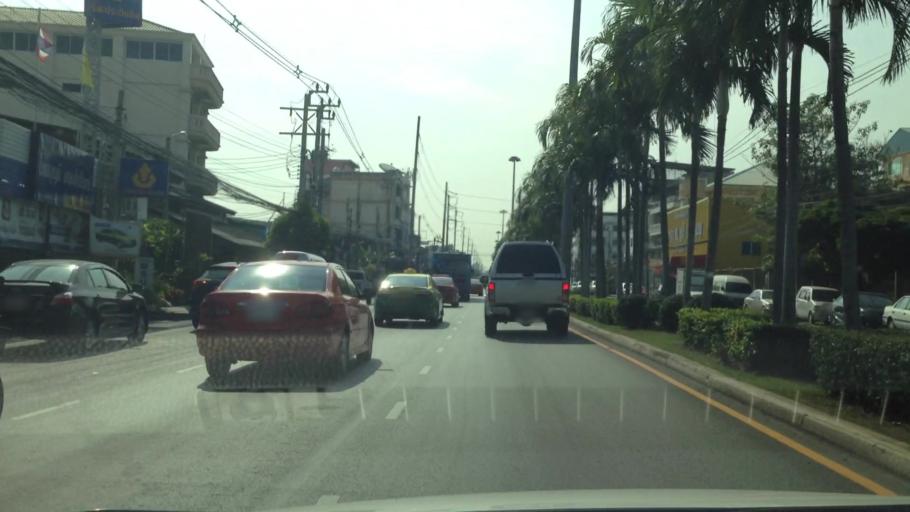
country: TH
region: Samut Prakan
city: Samut Prakan
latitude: 13.5854
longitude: 100.5996
